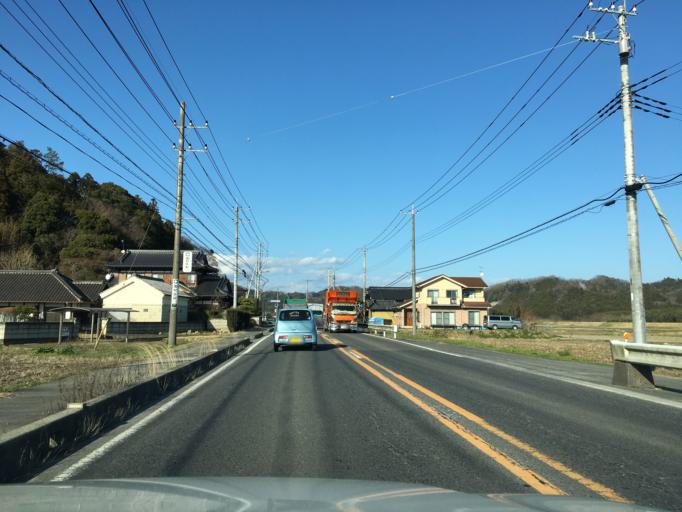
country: JP
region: Ibaraki
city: Omiya
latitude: 36.5874
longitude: 140.4098
